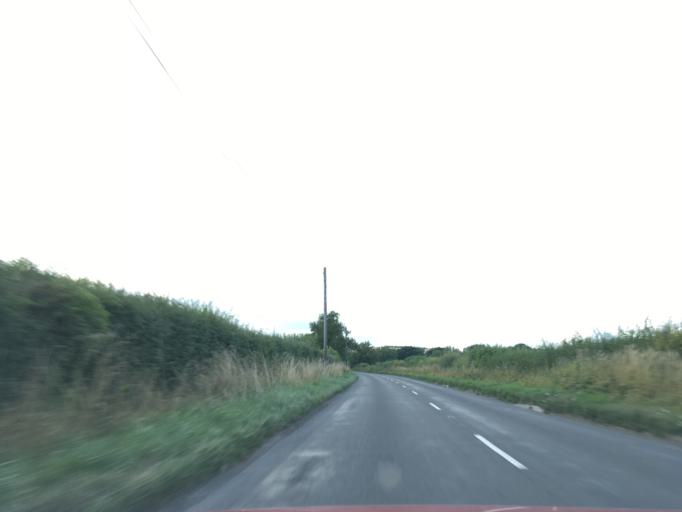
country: GB
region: England
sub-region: Wiltshire
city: Market Lavington
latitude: 51.3270
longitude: -1.9346
